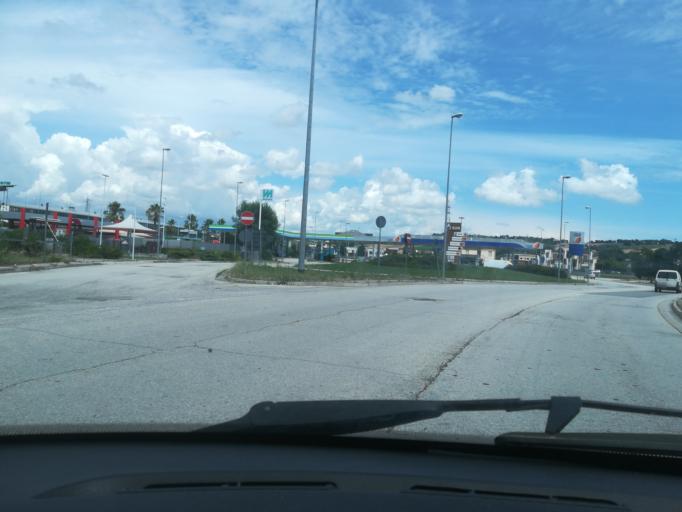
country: IT
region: The Marches
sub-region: Provincia di Macerata
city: Santa Maria Apparente
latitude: 43.2816
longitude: 13.6845
